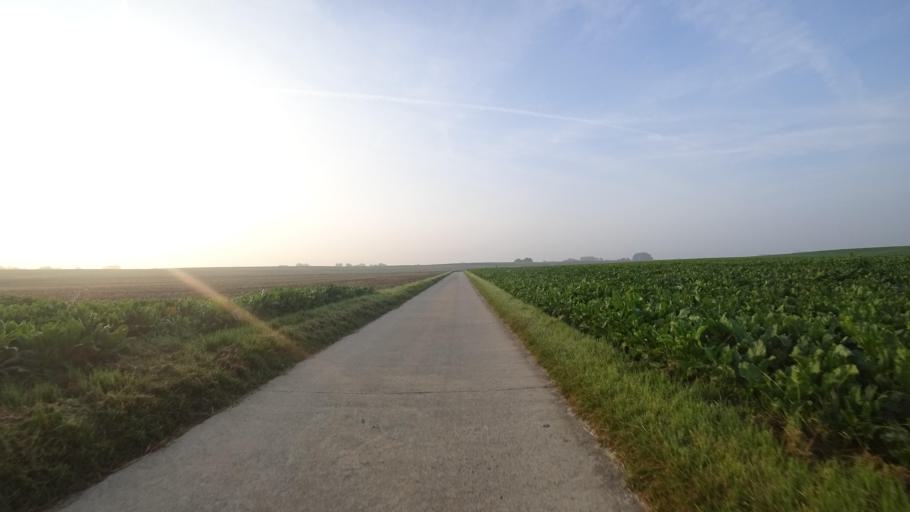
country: BE
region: Wallonia
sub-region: Province du Brabant Wallon
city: Walhain-Saint-Paul
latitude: 50.6407
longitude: 4.6932
